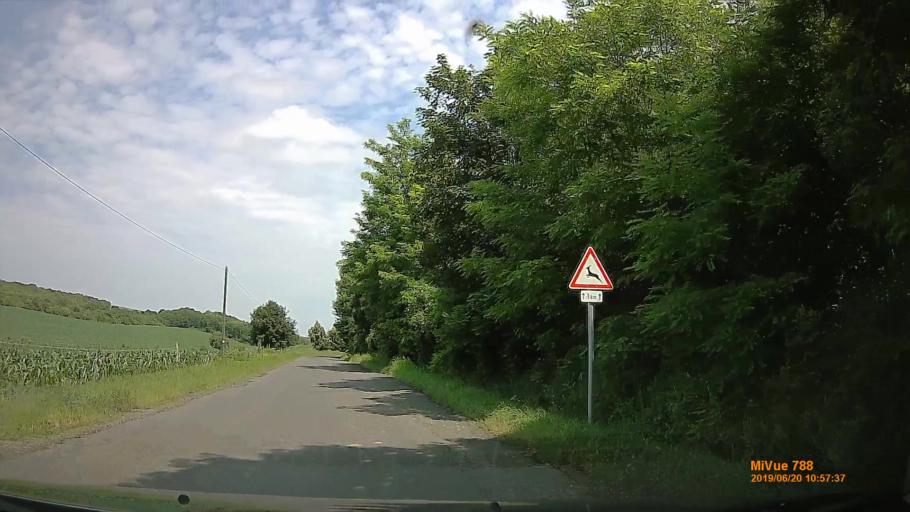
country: HU
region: Baranya
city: Mecseknadasd
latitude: 46.1535
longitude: 18.5199
